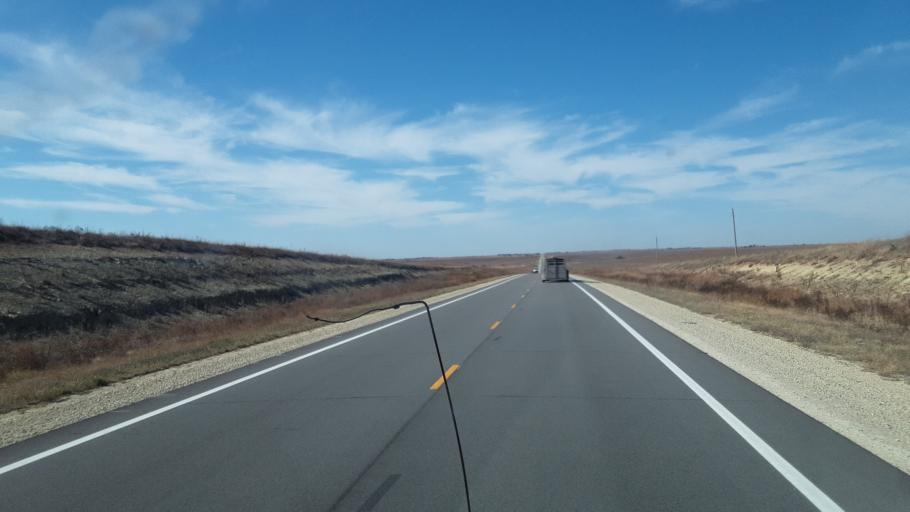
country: US
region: Kansas
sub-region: Chase County
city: Cottonwood Falls
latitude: 38.3626
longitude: -96.7384
